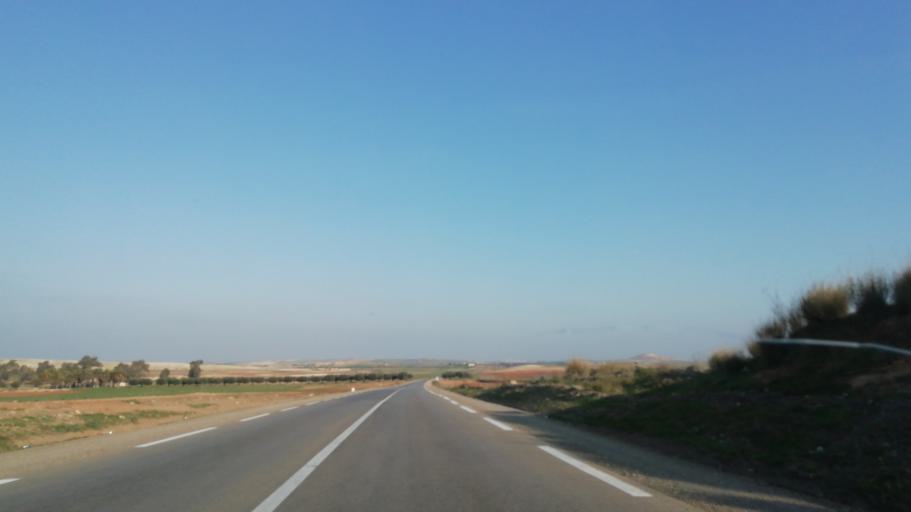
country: DZ
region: Sidi Bel Abbes
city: Sidi Bel Abbes
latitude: 35.1784
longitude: -0.8074
